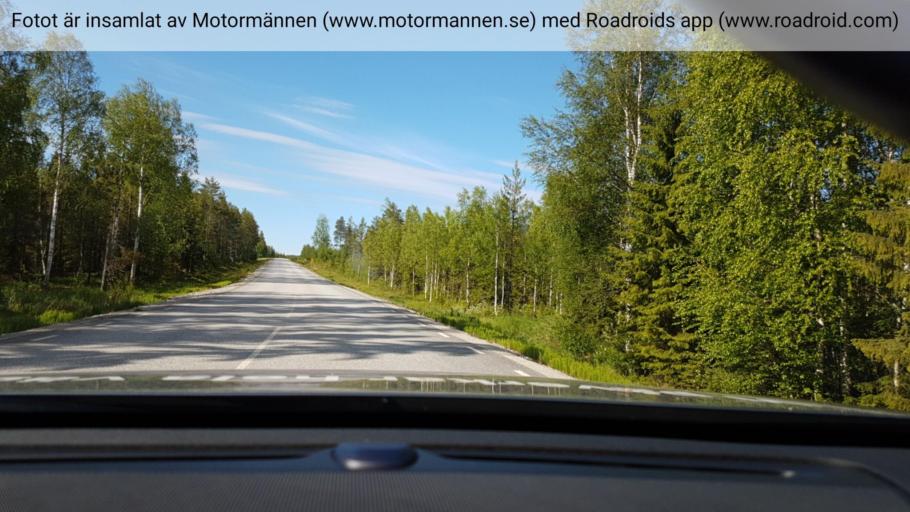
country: SE
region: Vaesterbotten
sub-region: Bjurholms Kommun
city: Bjurholm
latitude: 64.1541
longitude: 19.3543
